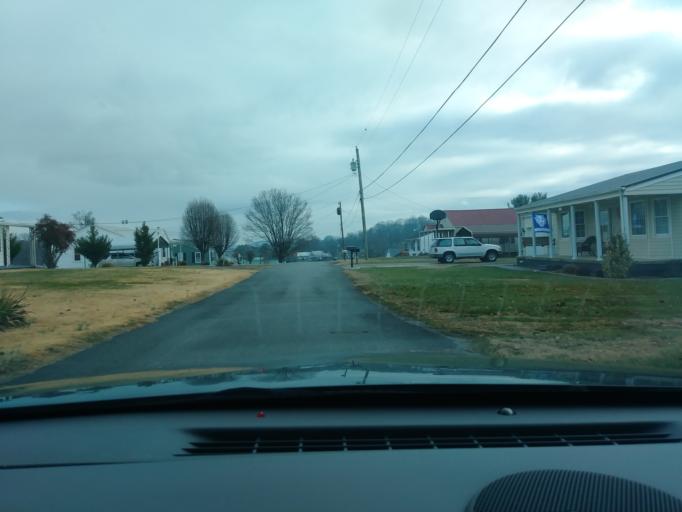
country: US
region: Tennessee
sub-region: Greene County
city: Greeneville
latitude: 36.1165
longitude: -82.8683
